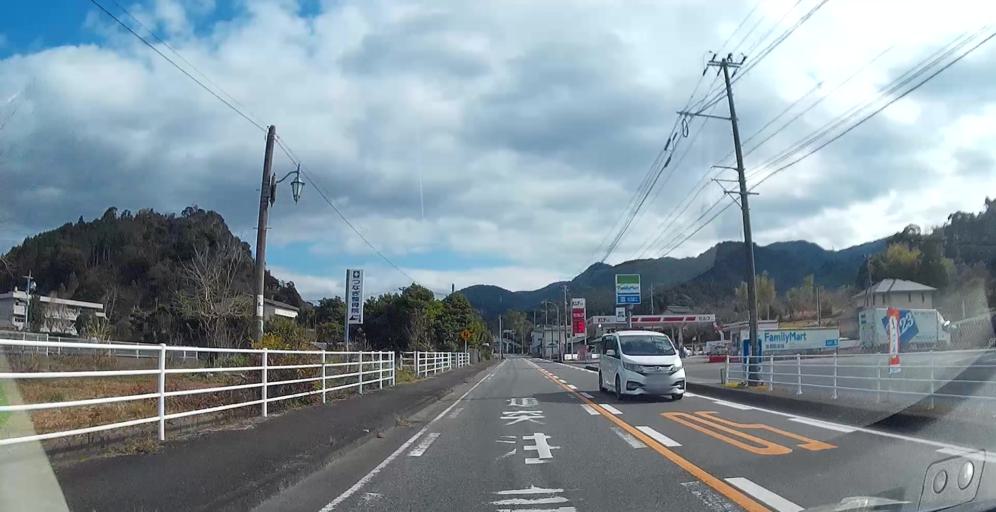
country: JP
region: Kumamoto
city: Minamata
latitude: 32.2322
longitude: 130.4540
